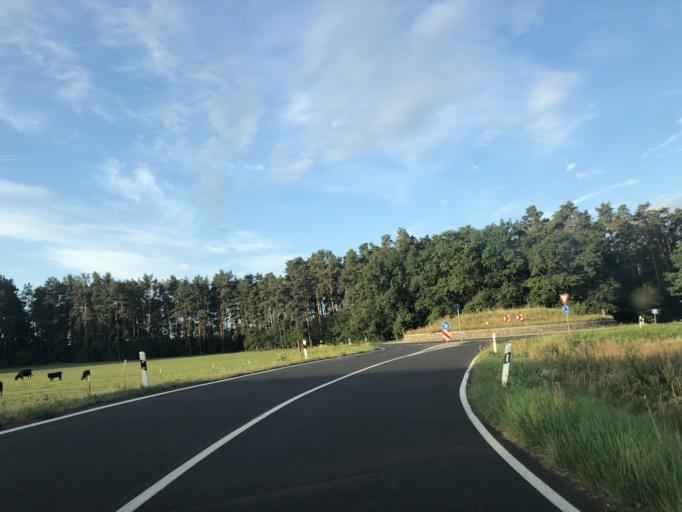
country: DE
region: Brandenburg
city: Mullrose
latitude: 52.2360
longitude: 14.3958
